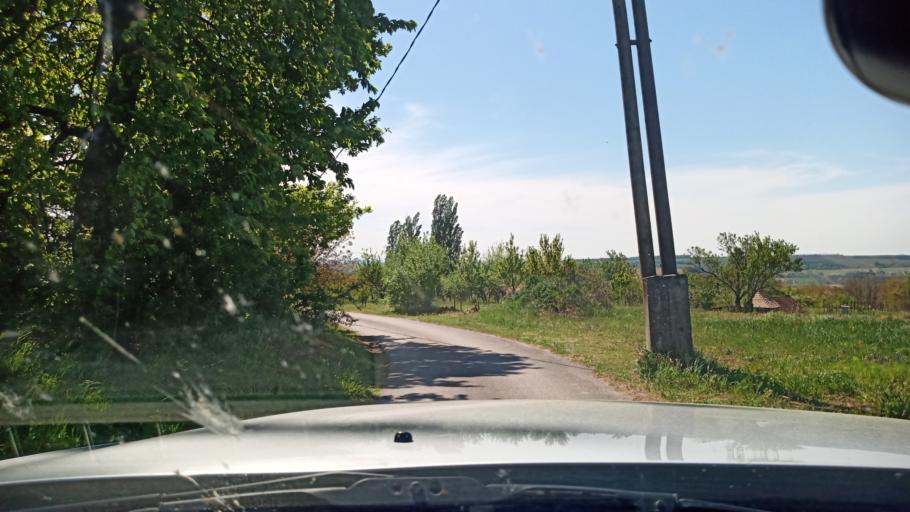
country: HU
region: Zala
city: Heviz
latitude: 46.7630
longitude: 17.1463
